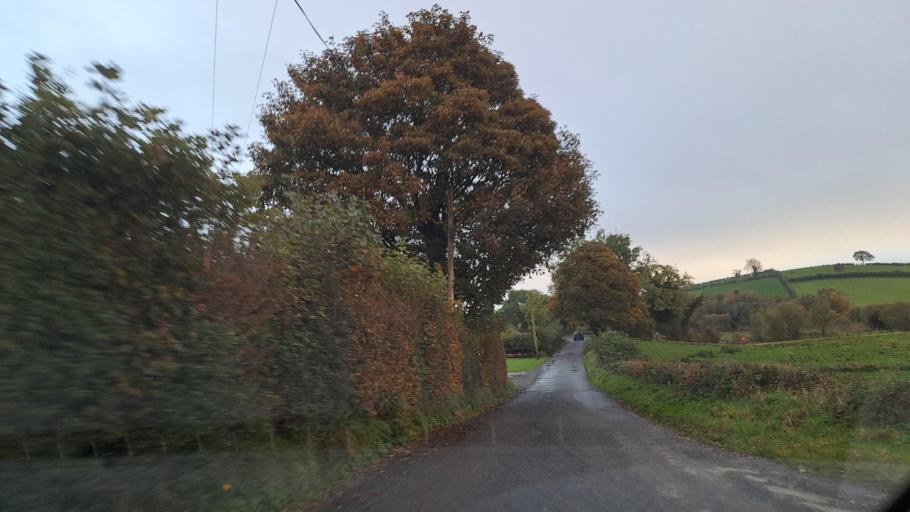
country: IE
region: Ulster
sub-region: County Monaghan
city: Carrickmacross
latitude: 53.9832
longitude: -6.6870
